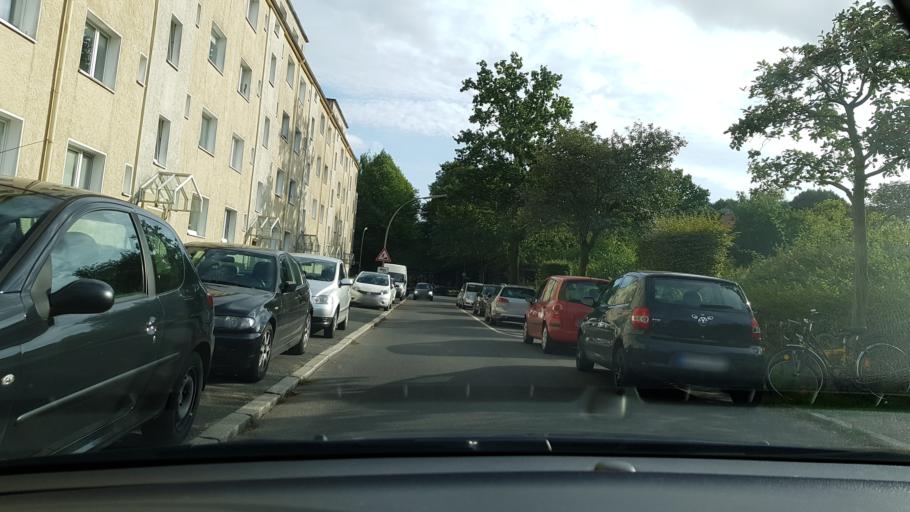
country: DE
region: Hamburg
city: Steilshoop
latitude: 53.5953
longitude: 10.0542
